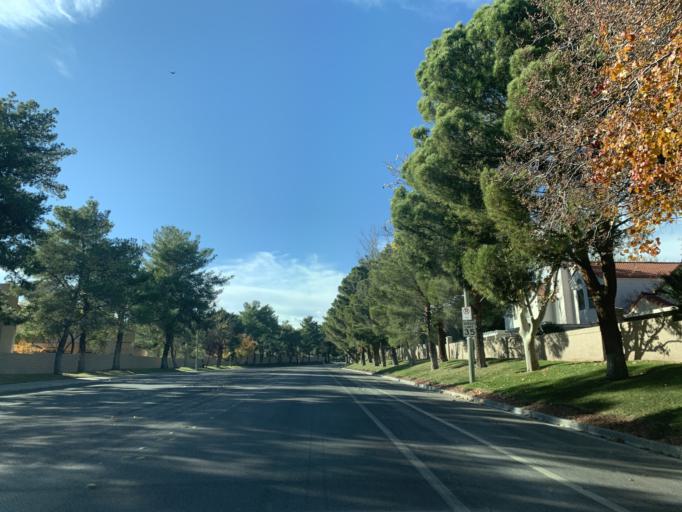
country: US
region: Nevada
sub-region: Clark County
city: Summerlin South
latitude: 36.1335
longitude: -115.3070
